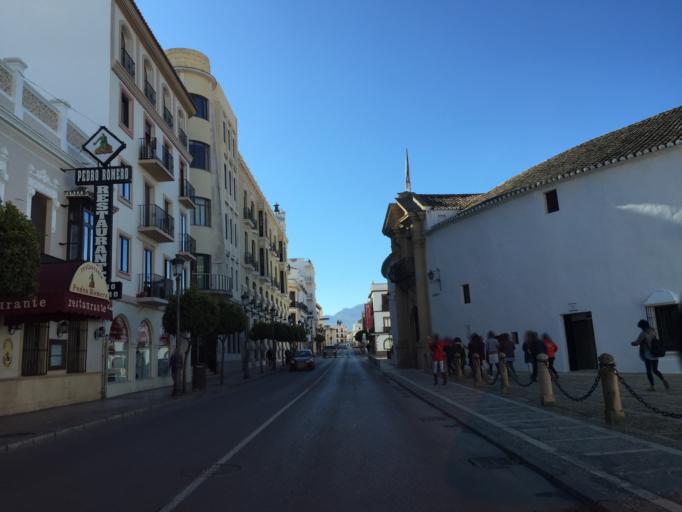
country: ES
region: Andalusia
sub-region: Provincia de Malaga
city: Ronda
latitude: 36.7429
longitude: -5.1668
